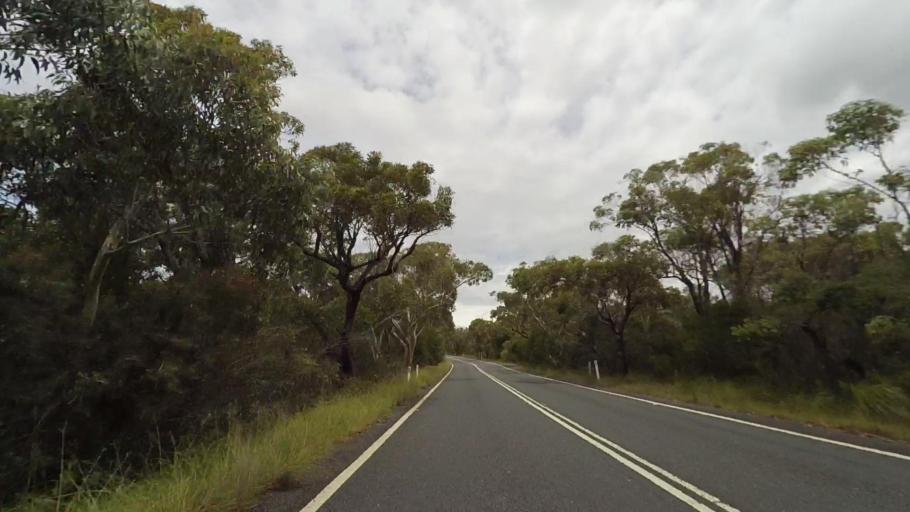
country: AU
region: New South Wales
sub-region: Sutherland Shire
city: Heathcote
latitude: -34.0993
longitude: 151.0591
